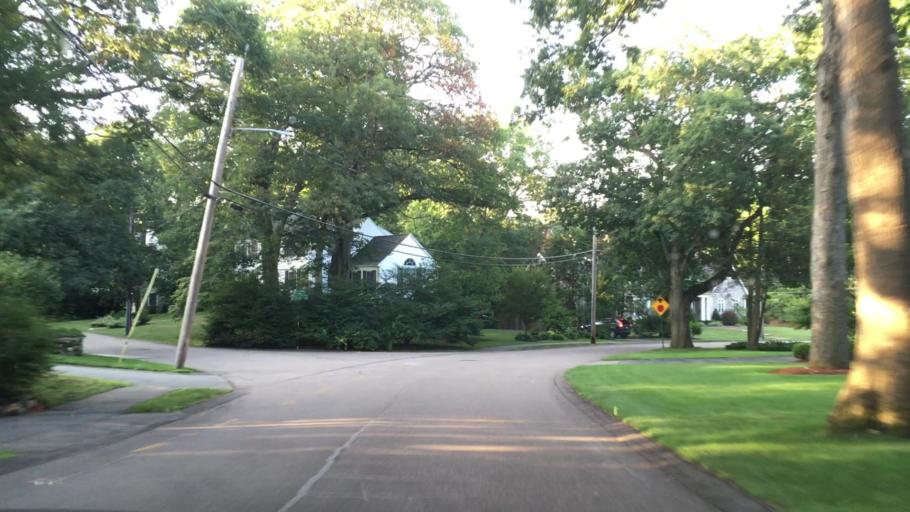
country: US
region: Massachusetts
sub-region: Norfolk County
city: Wellesley
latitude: 42.3117
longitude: -71.2918
